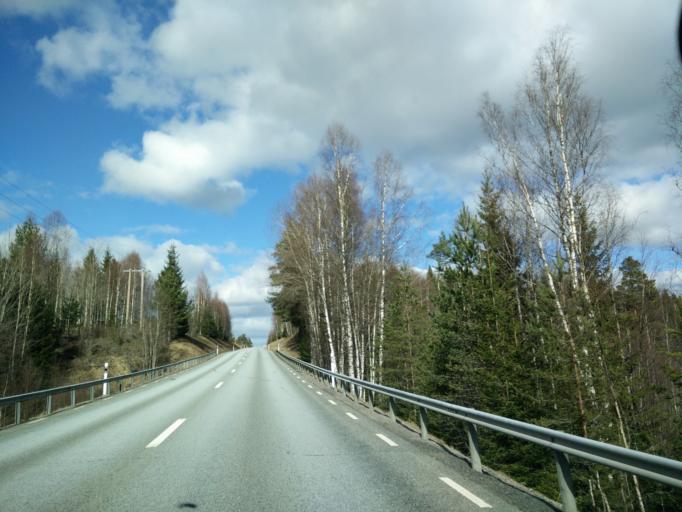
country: SE
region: Vaermland
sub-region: Munkfors Kommun
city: Munkfors
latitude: 59.9215
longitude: 13.5728
